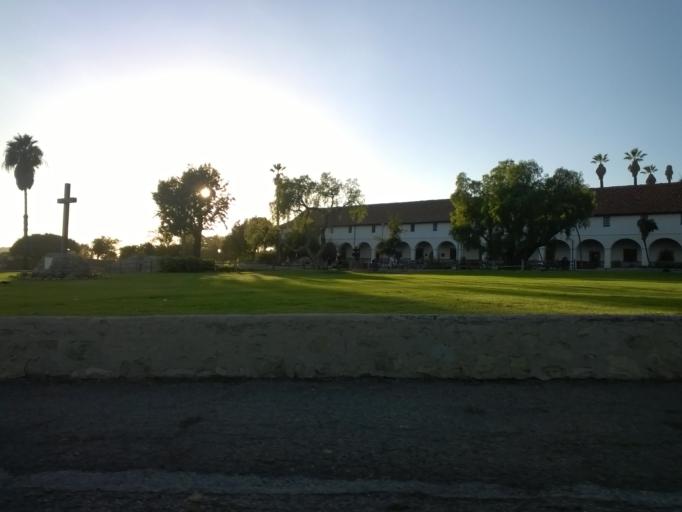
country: US
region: California
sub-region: Santa Barbara County
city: Mission Canyon
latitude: 34.4378
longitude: -119.7125
